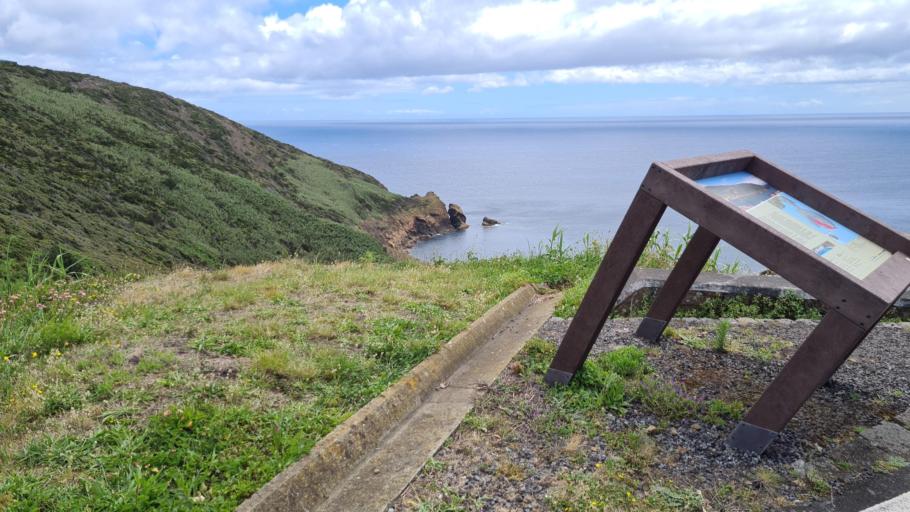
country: PT
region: Azores
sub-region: Horta
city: Horta
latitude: 38.5207
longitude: -28.6277
